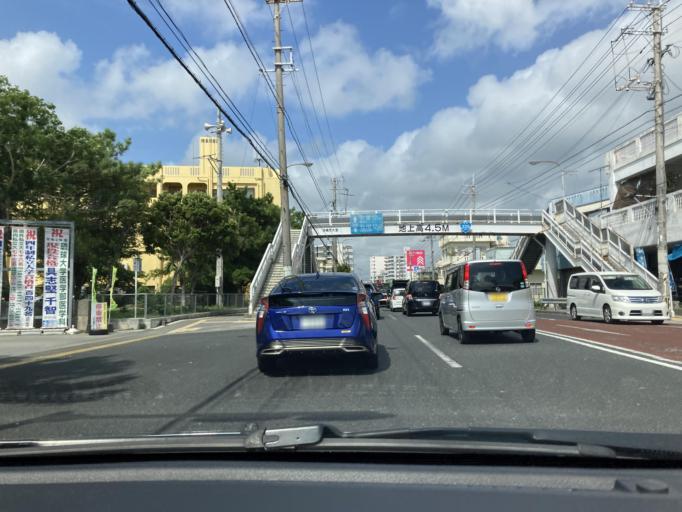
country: JP
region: Okinawa
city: Okinawa
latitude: 26.3333
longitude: 127.8201
